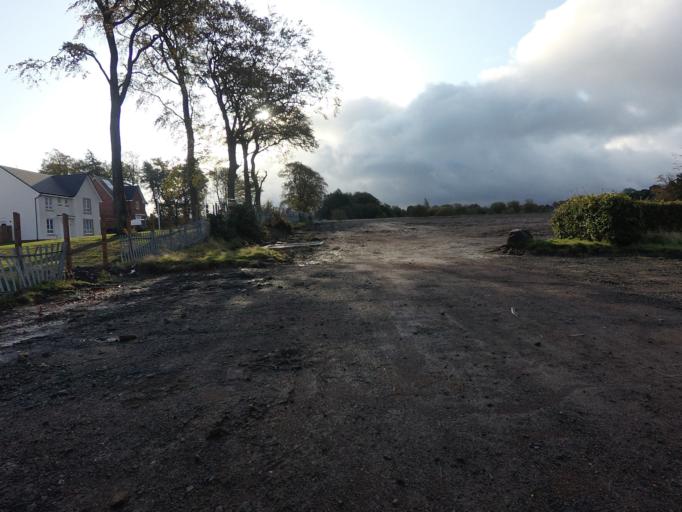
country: GB
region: Scotland
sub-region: West Lothian
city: West Calder
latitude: 55.8625
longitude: -3.5396
